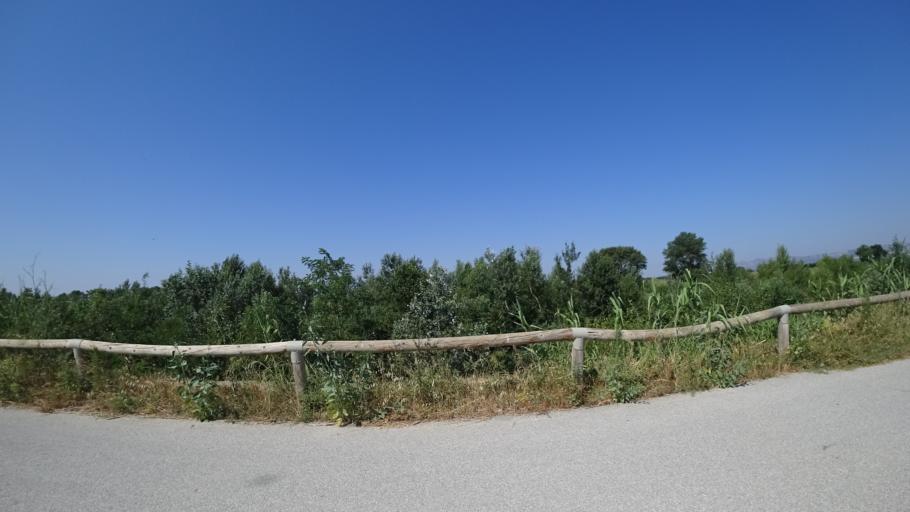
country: FR
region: Languedoc-Roussillon
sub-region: Departement des Pyrenees-Orientales
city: Pia
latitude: 42.7684
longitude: 2.9114
